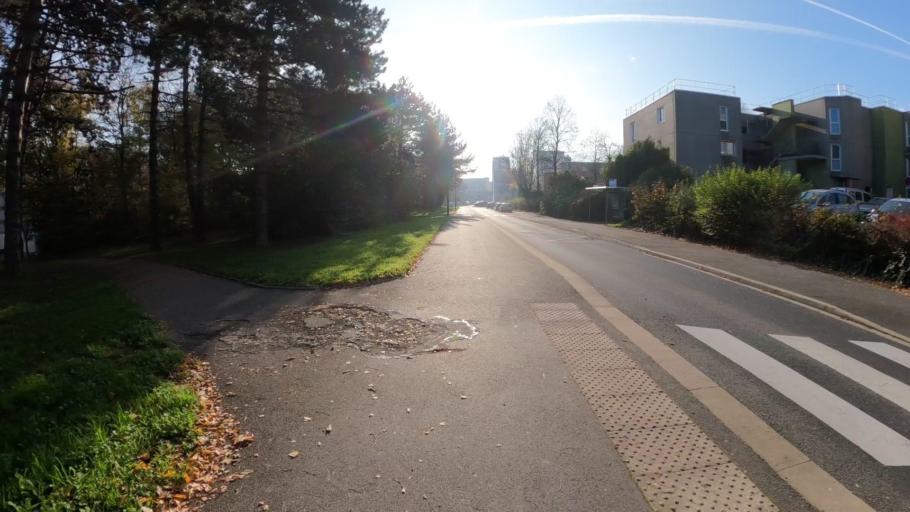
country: FR
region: Lower Normandy
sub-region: Departement du Calvados
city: Herouville-Saint-Clair
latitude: 49.2059
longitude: -0.3348
